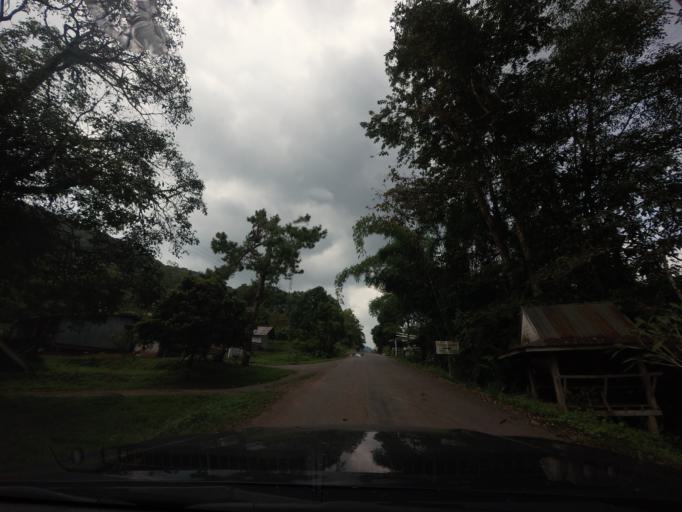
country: TH
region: Nan
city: Bo Kluea
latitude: 19.2722
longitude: 101.1781
